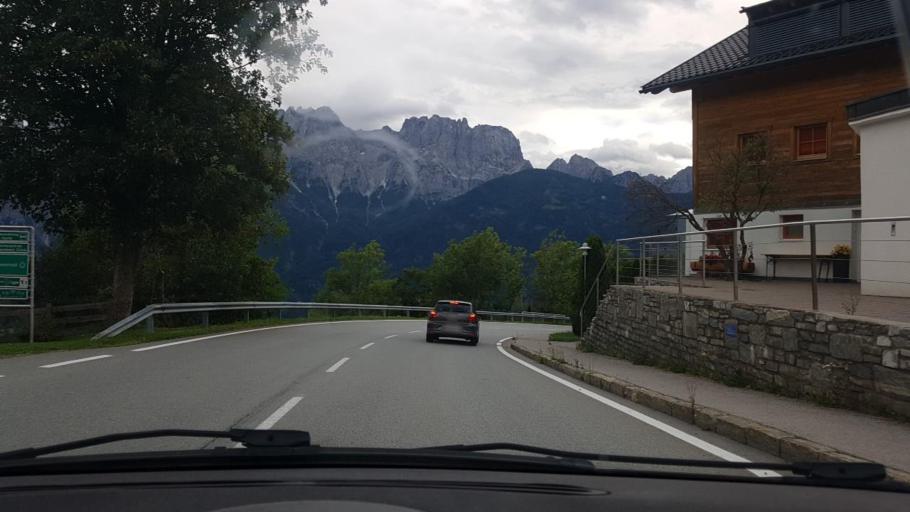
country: AT
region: Tyrol
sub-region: Politischer Bezirk Lienz
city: Dolsach
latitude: 46.8380
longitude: 12.8441
